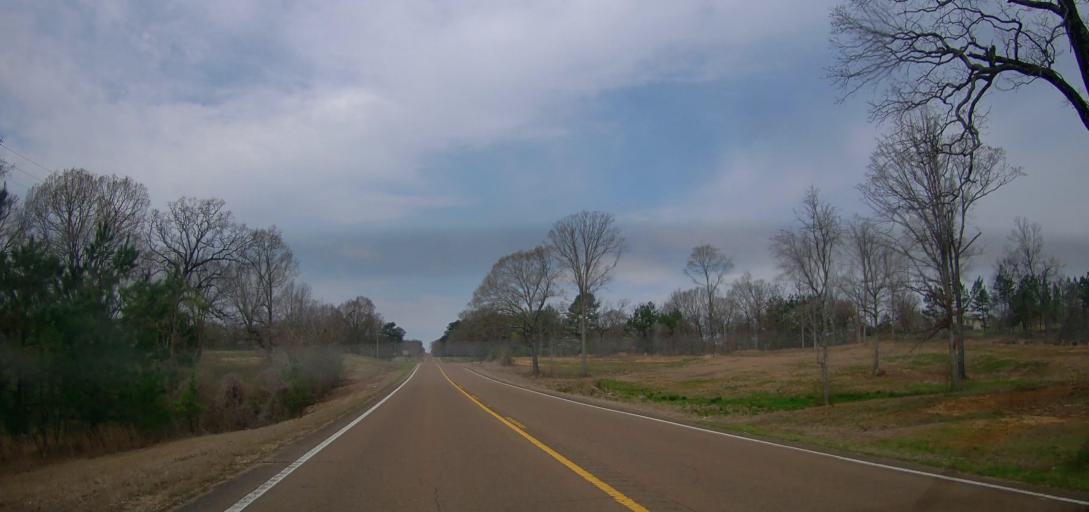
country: US
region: Mississippi
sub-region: Marshall County
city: Byhalia
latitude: 34.8313
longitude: -89.5741
